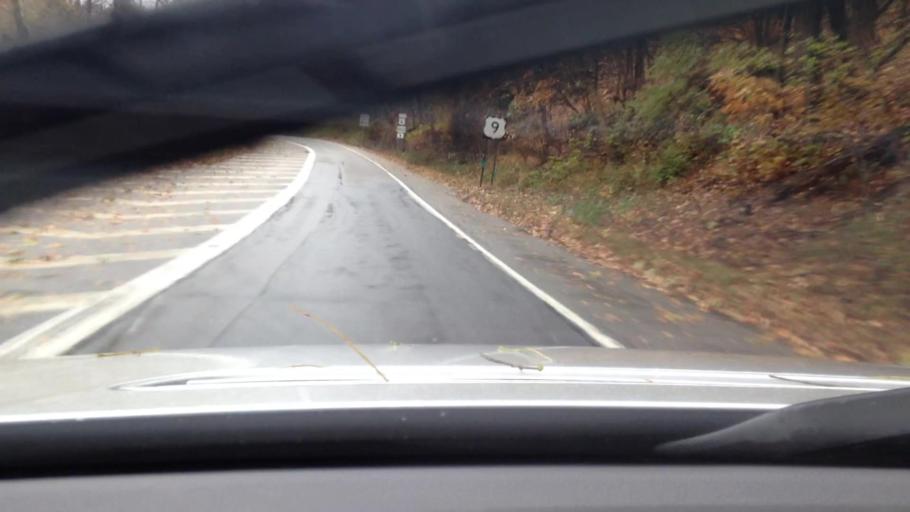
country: US
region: New York
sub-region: Westchester County
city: Peekskill
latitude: 41.3092
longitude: -73.9316
